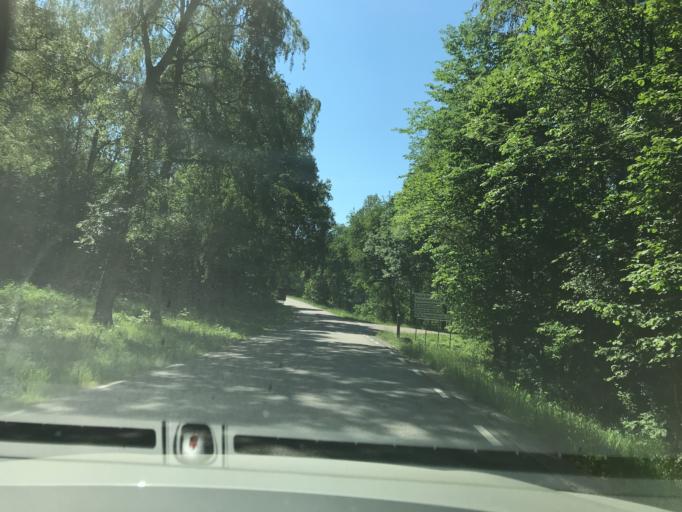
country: SE
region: Vaestra Goetaland
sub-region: Gotene Kommun
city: Goetene
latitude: 58.6225
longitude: 13.4091
